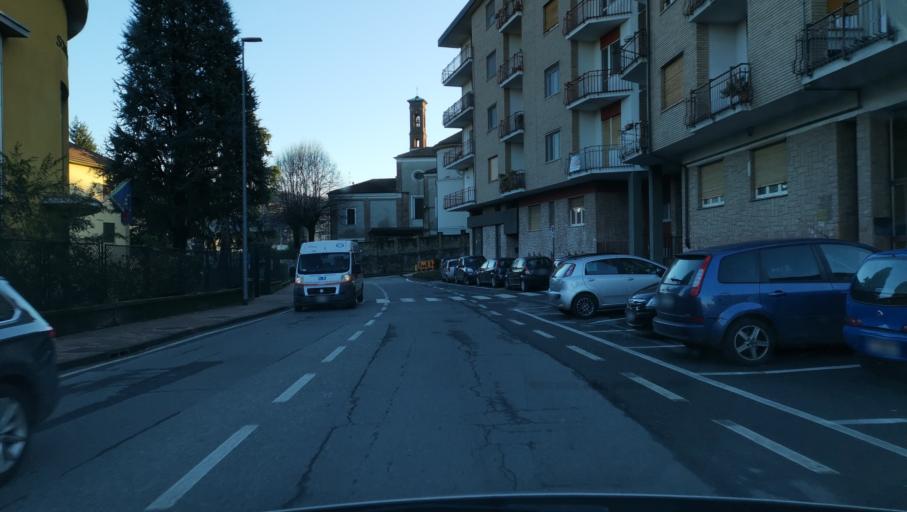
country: IT
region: Piedmont
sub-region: Provincia di Torino
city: Gassino Torinese
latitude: 45.1298
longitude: 7.8256
